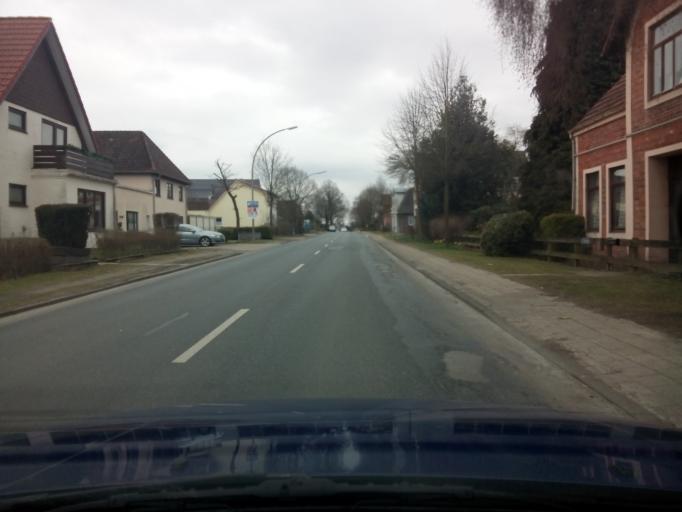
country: DE
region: Lower Saxony
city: Osterholz-Scharmbeck
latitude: 53.2317
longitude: 8.8092
